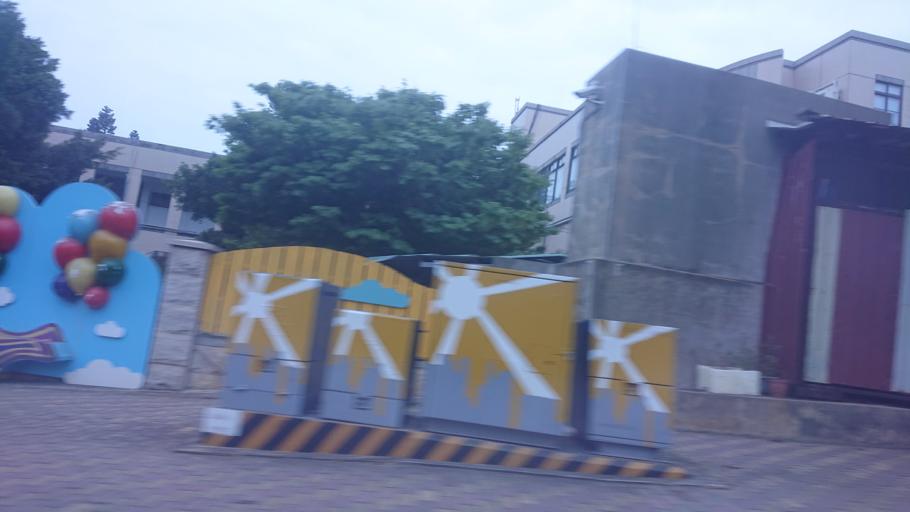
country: TW
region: Fukien
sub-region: Kinmen
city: Jincheng
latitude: 24.4316
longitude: 118.3135
